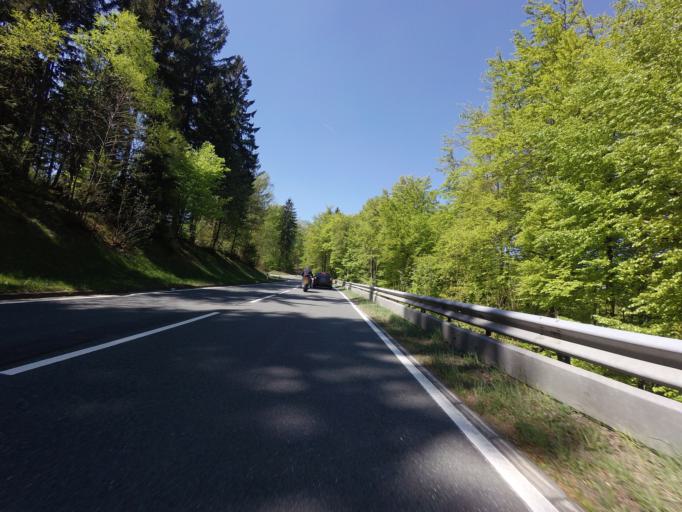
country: DE
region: North Rhine-Westphalia
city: Hilchenbach
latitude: 50.9662
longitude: 8.1393
